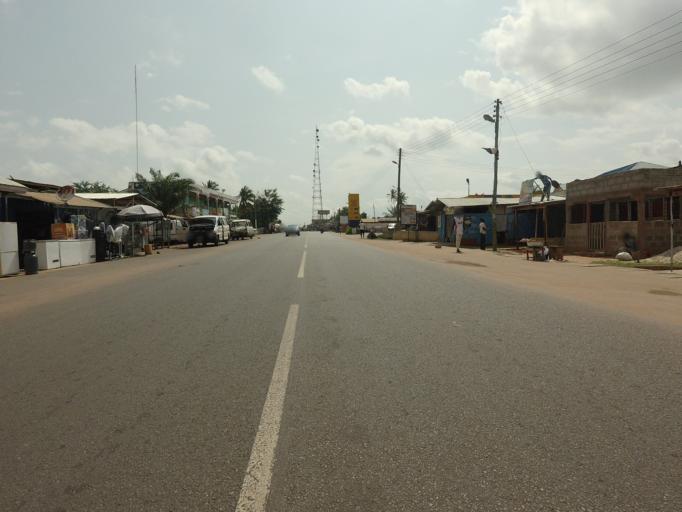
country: TG
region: Maritime
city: Lome
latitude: 6.2319
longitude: 1.0031
